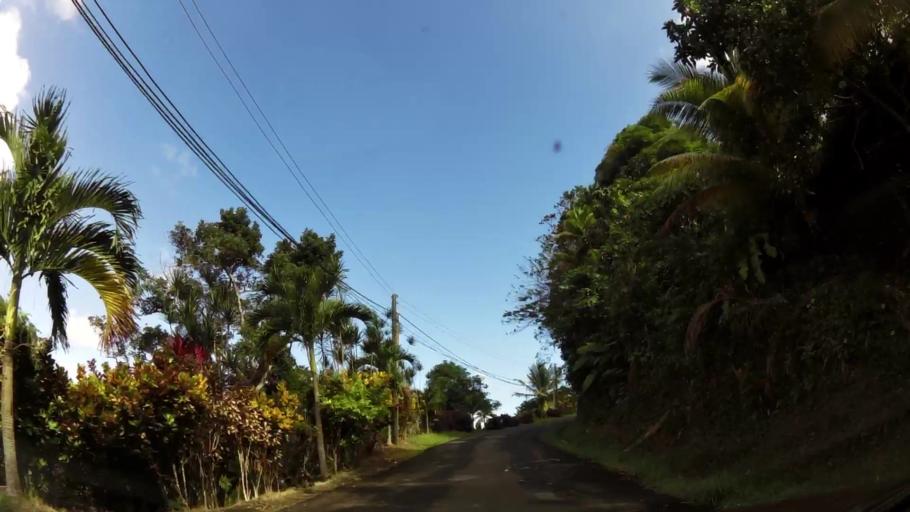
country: DM
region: Saint Andrew
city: Marigot
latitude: 15.5151
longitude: -61.2697
